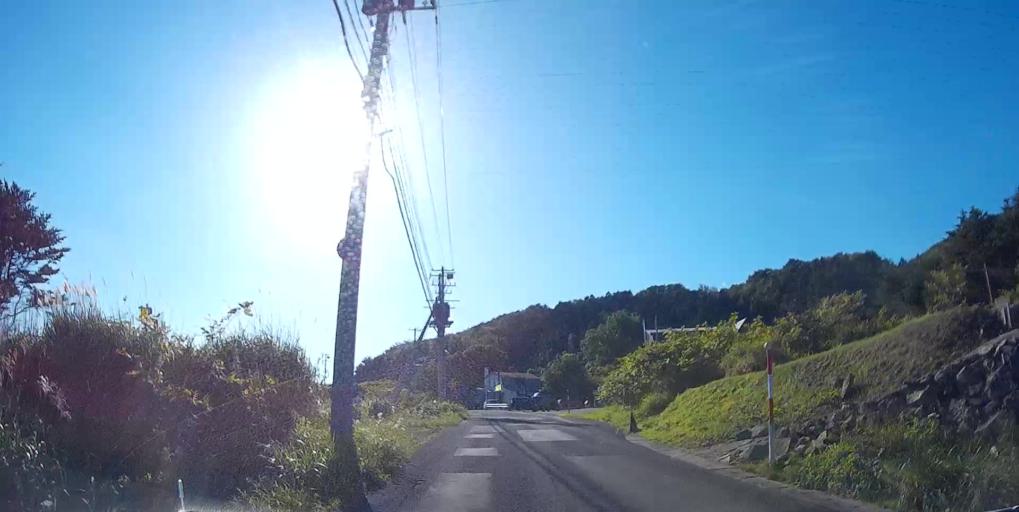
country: JP
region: Hokkaido
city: Kamiiso
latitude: 42.2300
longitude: 139.8079
